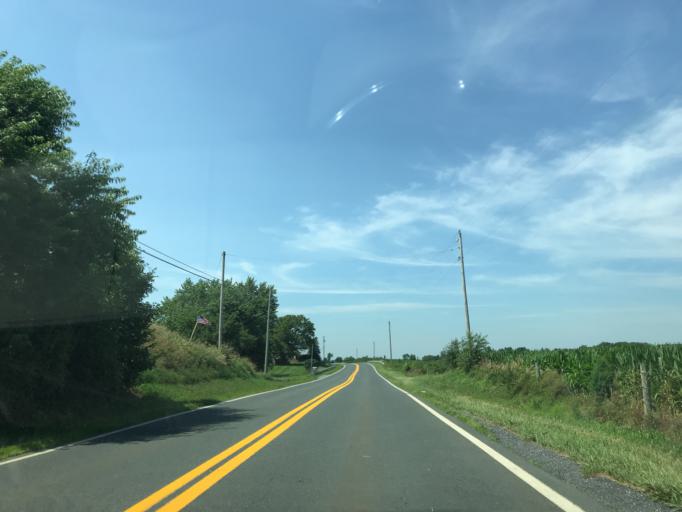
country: US
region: Maryland
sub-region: Carroll County
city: New Windsor
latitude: 39.6038
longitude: -77.1230
